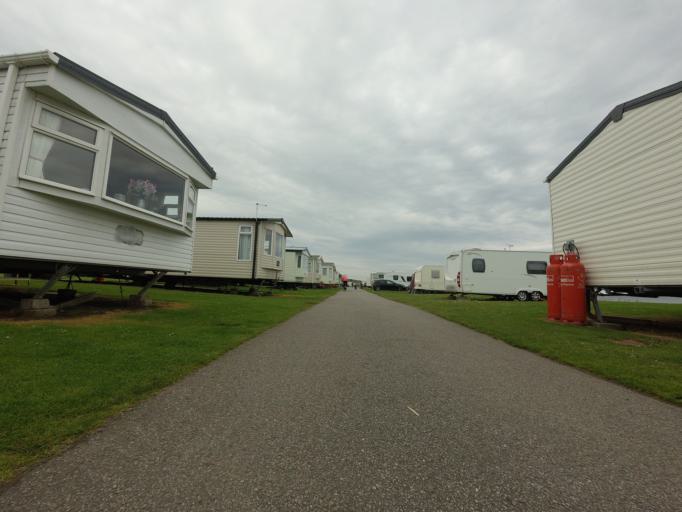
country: GB
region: Scotland
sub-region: Aberdeenshire
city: Banff
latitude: 57.6708
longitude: -2.5551
